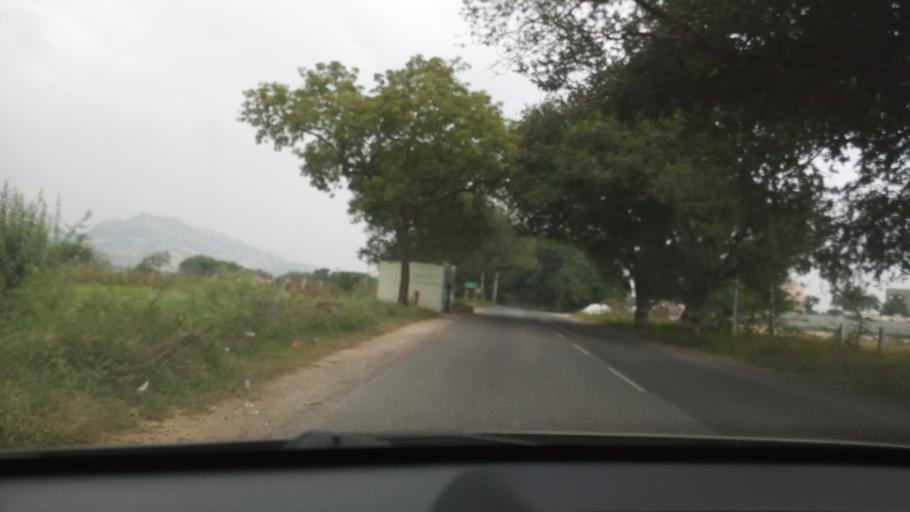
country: IN
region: Andhra Pradesh
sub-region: Chittoor
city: Madanapalle
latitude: 13.6516
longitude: 78.8141
